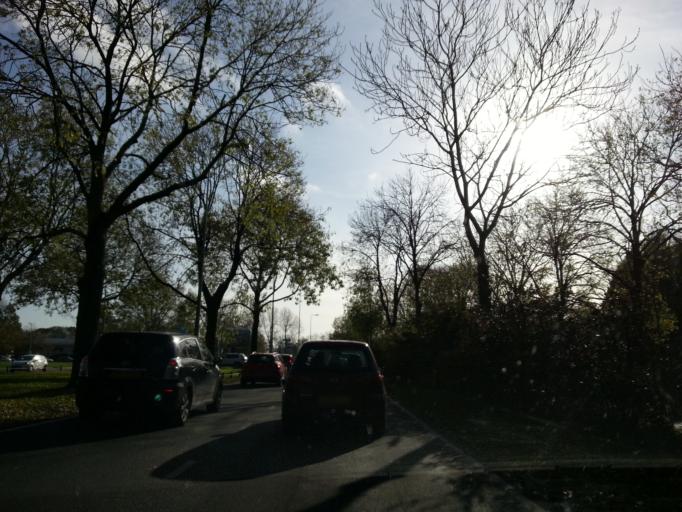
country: NL
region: South Holland
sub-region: Gemeente Leiden
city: Leiden
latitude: 52.1408
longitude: 4.4777
